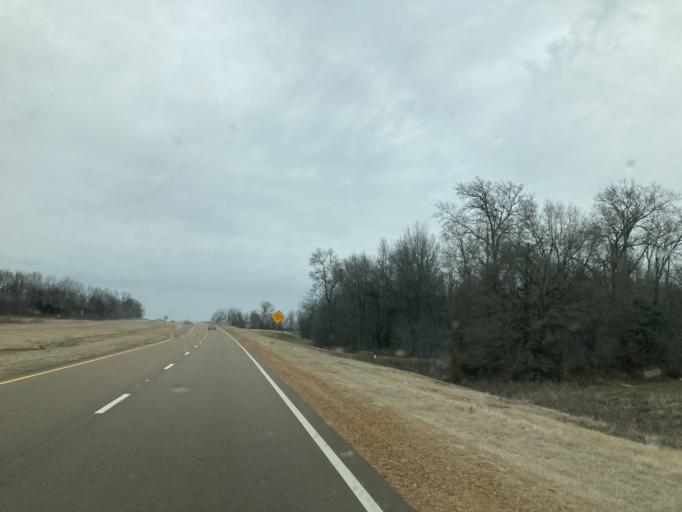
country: US
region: Mississippi
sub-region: Humphreys County
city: Belzoni
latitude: 33.0497
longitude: -90.4674
